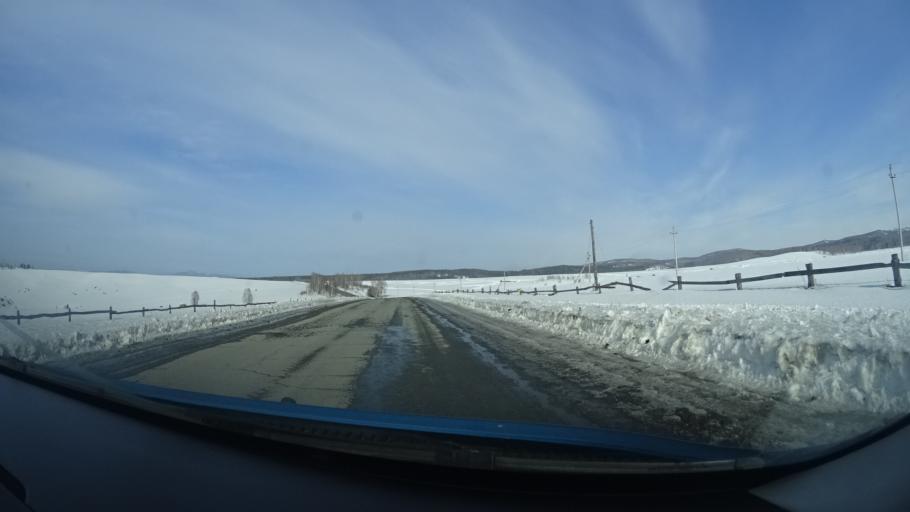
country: RU
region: Bashkortostan
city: Lomovka
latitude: 53.8051
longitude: 58.2703
